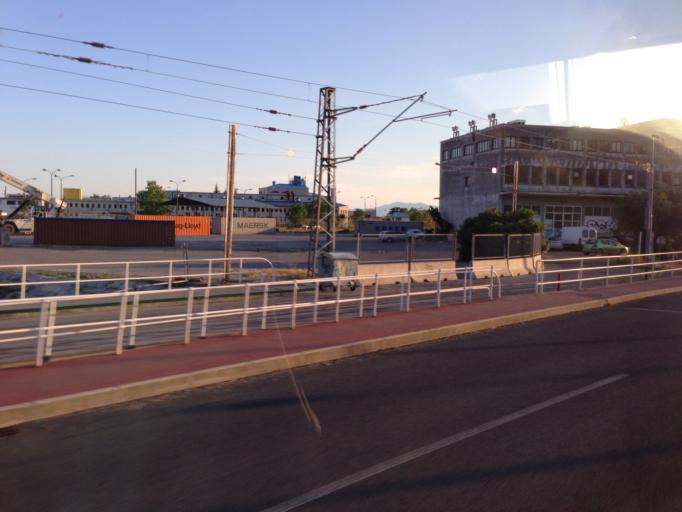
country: HR
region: Primorsko-Goranska
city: Drenova
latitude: 45.3236
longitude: 14.4497
